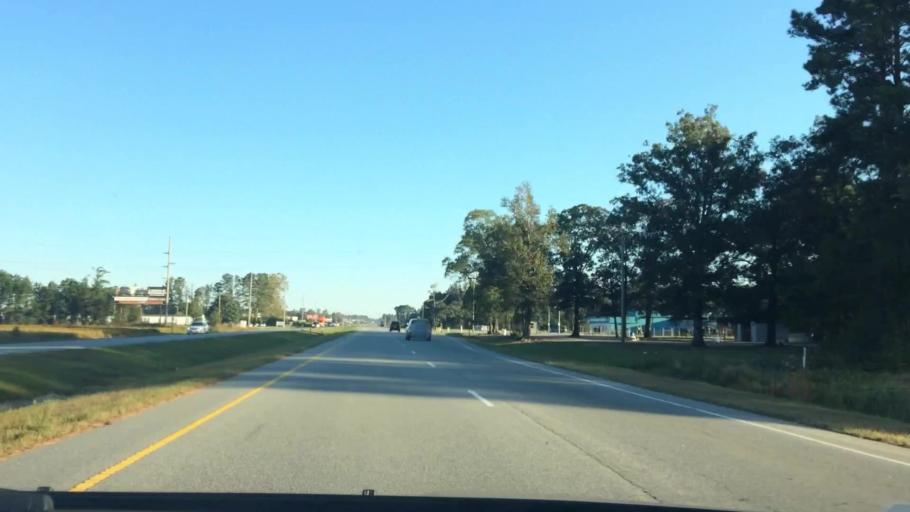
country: US
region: North Carolina
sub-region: Pitt County
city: Grifton
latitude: 35.4216
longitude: -77.4341
